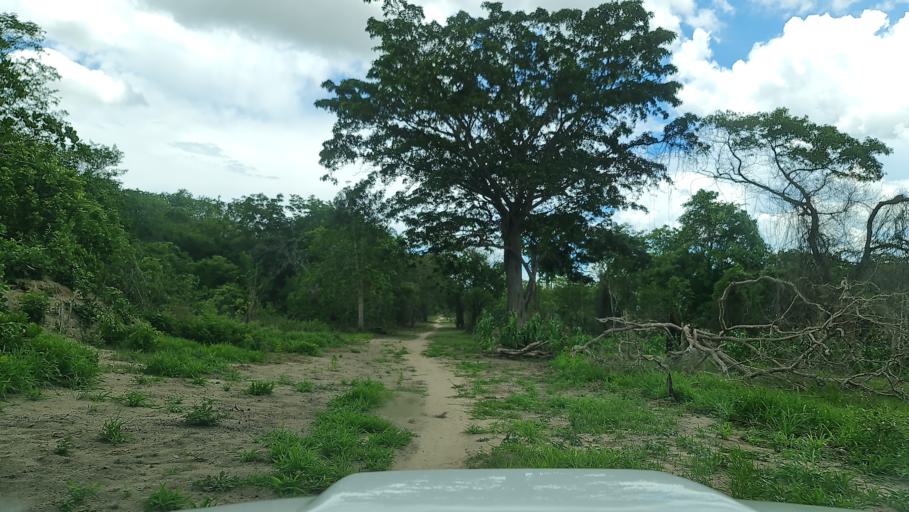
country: MZ
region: Nampula
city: Ilha de Mocambique
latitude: -15.4996
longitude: 40.1711
